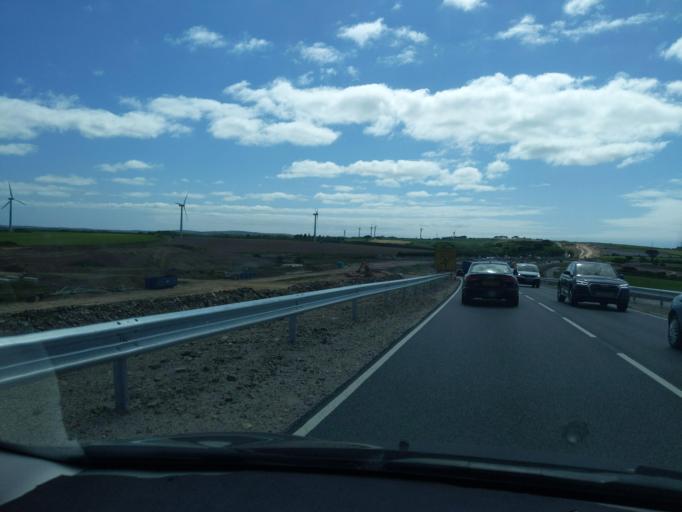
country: GB
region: England
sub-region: Cornwall
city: Perranporth
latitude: 50.2990
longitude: -5.1185
